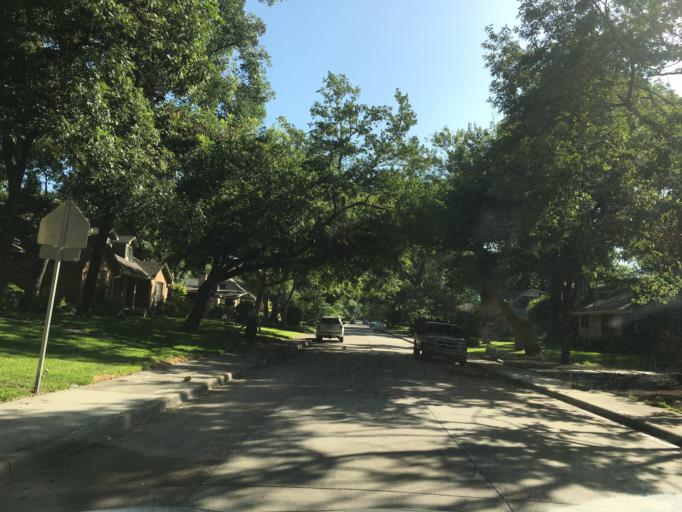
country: US
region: Texas
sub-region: Dallas County
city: Richardson
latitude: 32.8749
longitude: -96.7257
